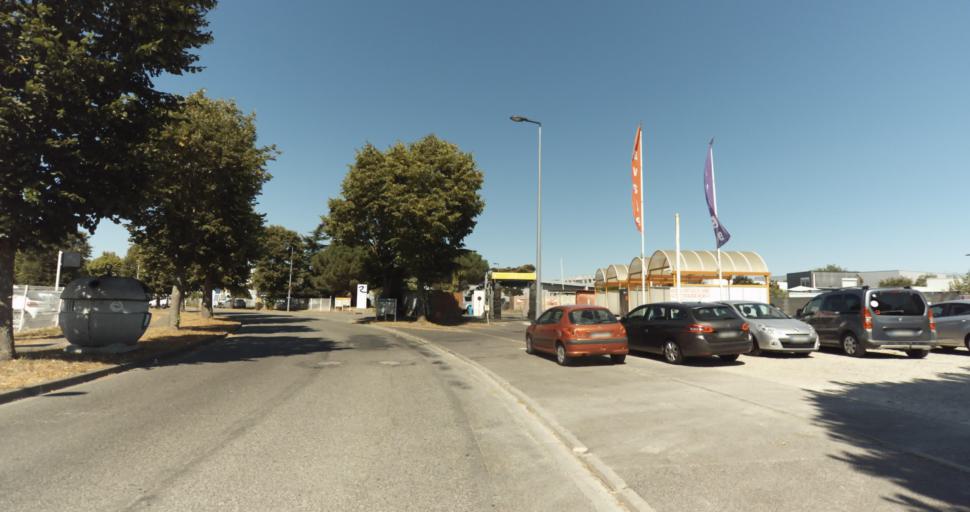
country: FR
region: Midi-Pyrenees
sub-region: Departement de la Haute-Garonne
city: Montrabe
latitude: 43.6392
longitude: 1.4999
